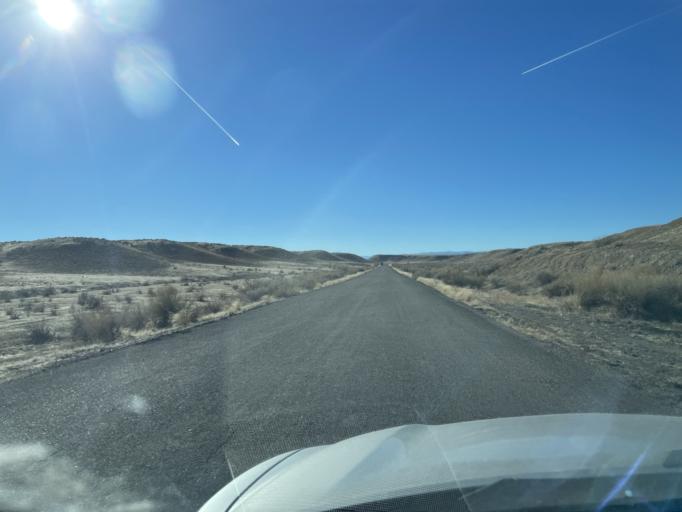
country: US
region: Colorado
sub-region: Mesa County
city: Loma
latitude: 39.2059
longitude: -109.0963
